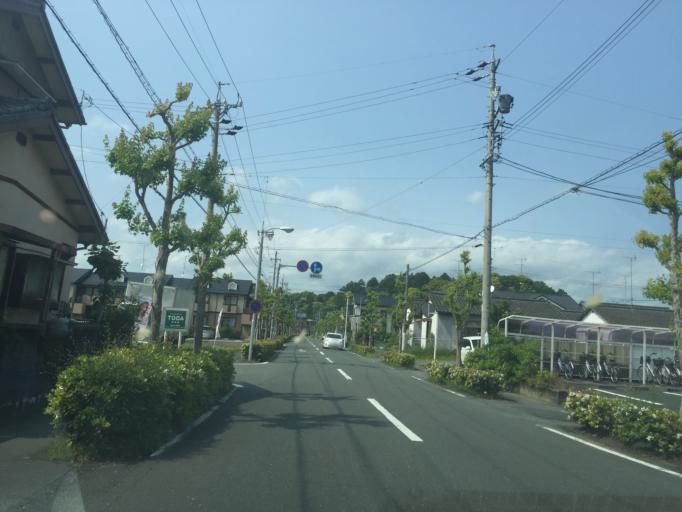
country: JP
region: Shizuoka
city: Kakegawa
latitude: 34.7791
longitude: 138.0164
